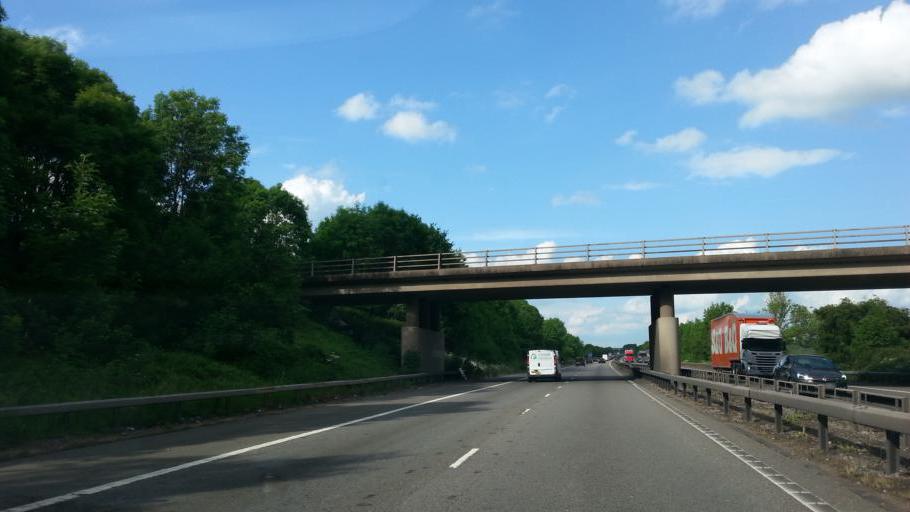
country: GB
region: England
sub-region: Derbyshire
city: Netherseal
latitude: 52.6599
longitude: -1.5790
